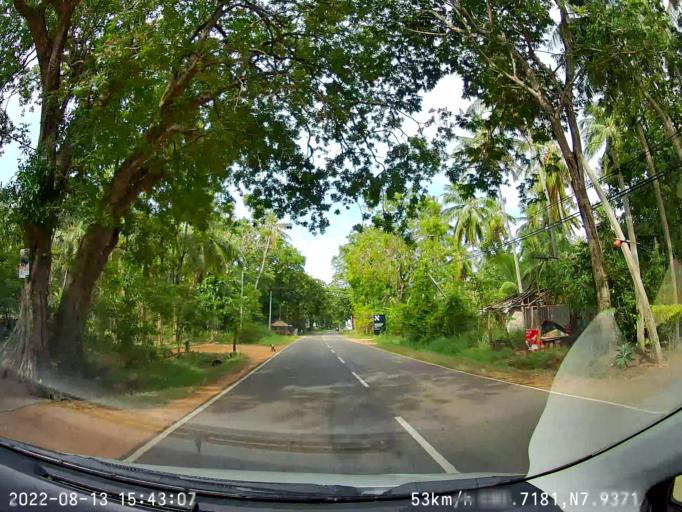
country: LK
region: Central
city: Sigiriya
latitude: 7.9372
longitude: 80.7184
